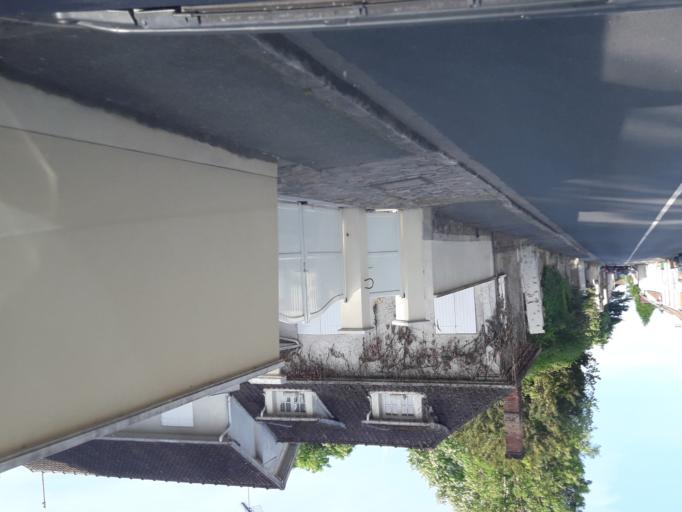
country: FR
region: Ile-de-France
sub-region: Departement de l'Essonne
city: Saint-Vrain
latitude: 48.5413
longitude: 2.3368
